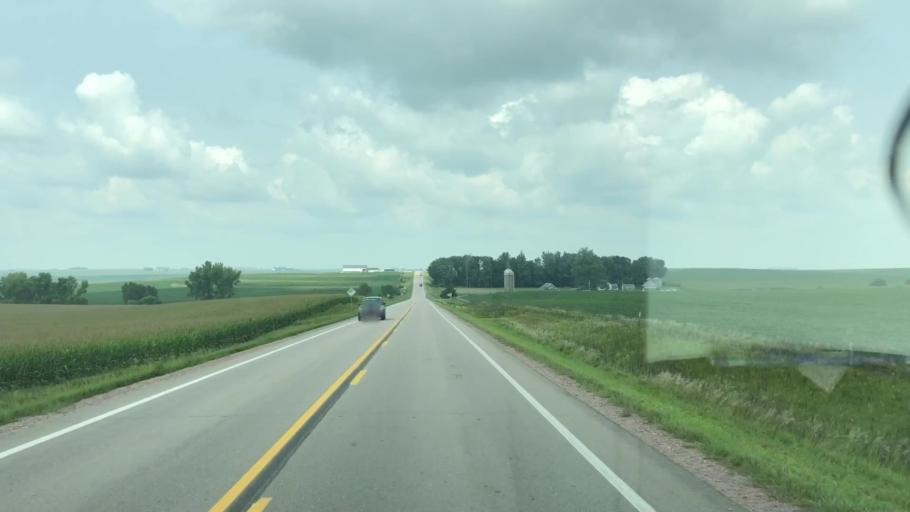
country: US
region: Iowa
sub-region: Plymouth County
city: Kingsley
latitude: 42.5940
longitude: -95.9573
